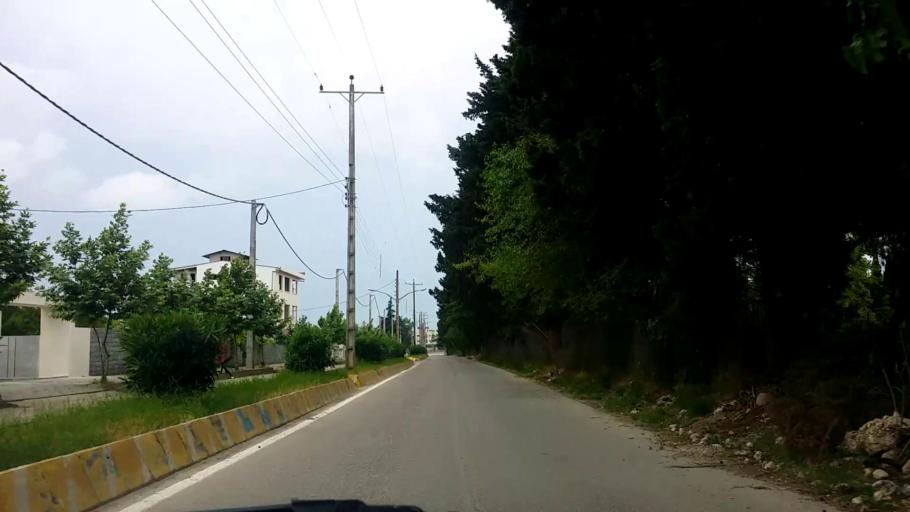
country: IR
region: Mazandaran
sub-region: Nowshahr
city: Nowshahr
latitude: 36.6345
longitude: 51.5026
